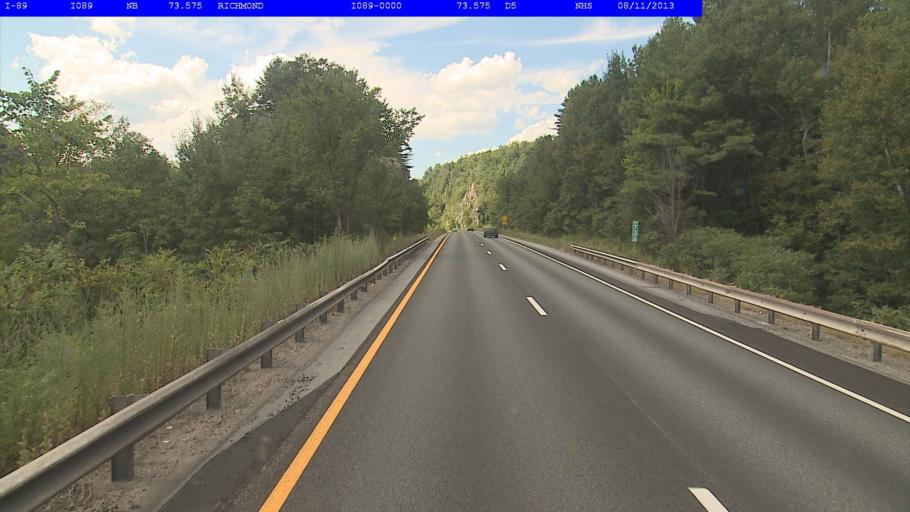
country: US
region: Vermont
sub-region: Chittenden County
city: Jericho
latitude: 44.3859
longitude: -72.9356
